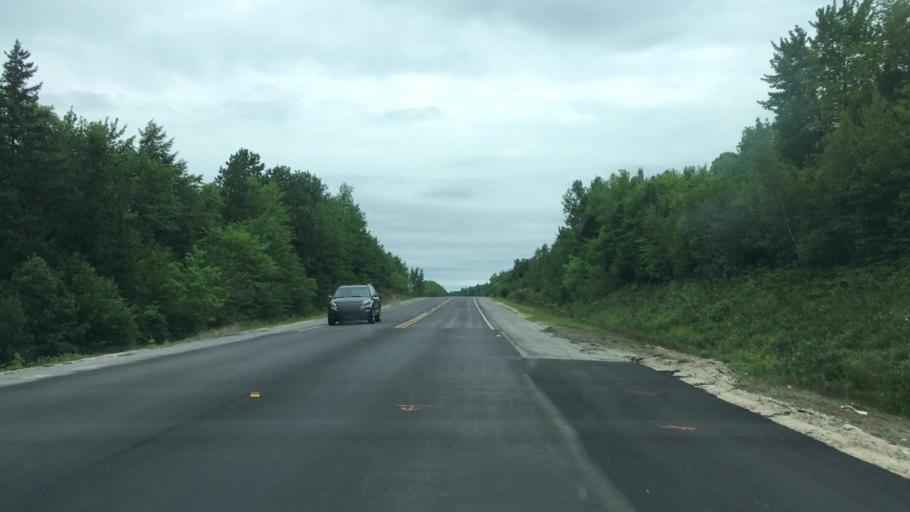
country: US
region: Maine
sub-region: Washington County
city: Cherryfield
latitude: 44.8863
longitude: -67.8568
